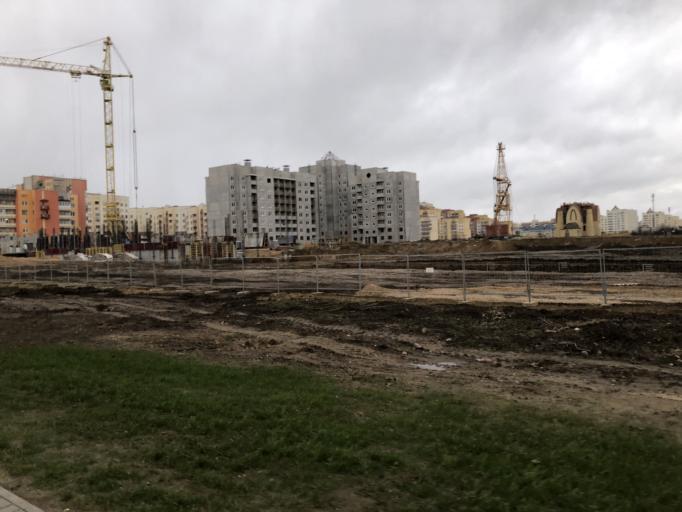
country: BY
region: Grodnenskaya
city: Hrodna
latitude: 53.7078
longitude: 23.8400
